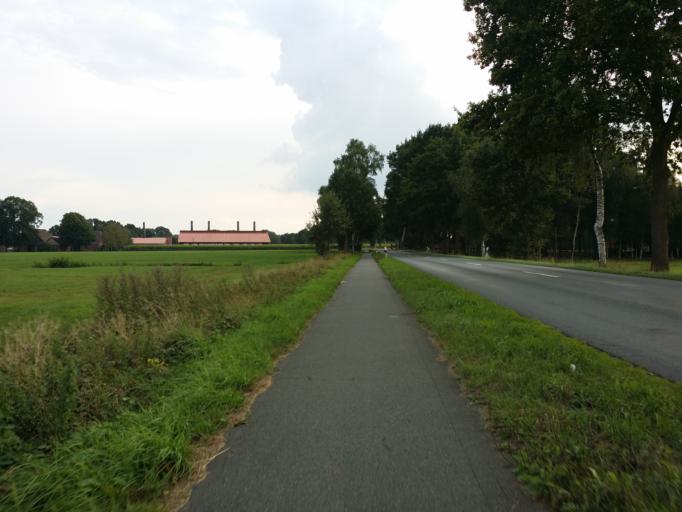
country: DE
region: Lower Saxony
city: Bremervorde
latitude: 53.4623
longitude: 9.1198
